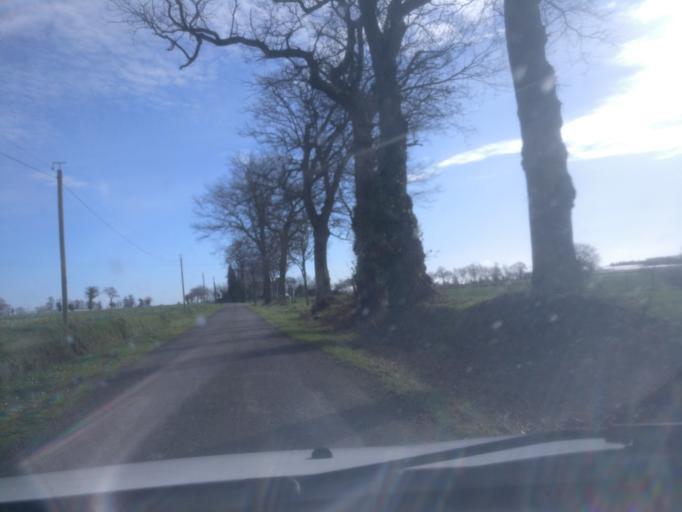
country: FR
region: Brittany
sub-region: Departement d'Ille-et-Vilaine
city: Antrain
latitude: 48.4484
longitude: -1.4833
